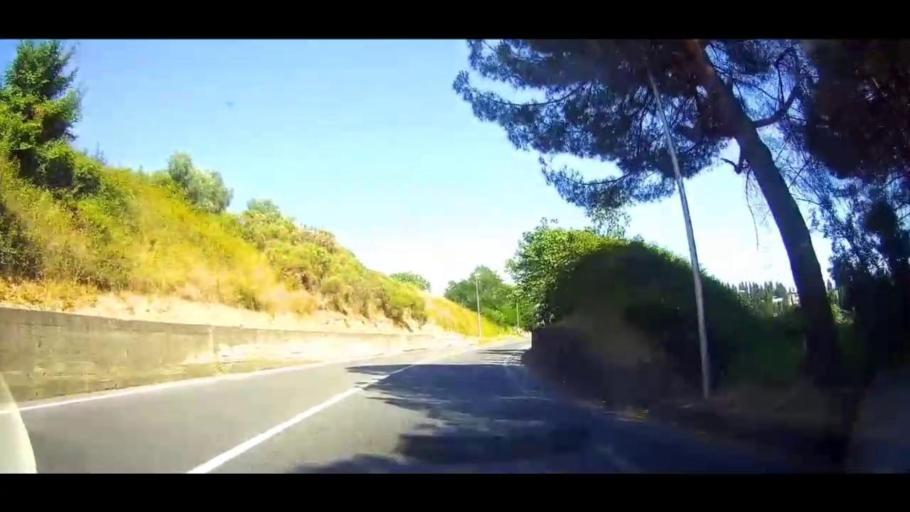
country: IT
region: Calabria
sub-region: Provincia di Cosenza
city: Cosenza
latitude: 39.2937
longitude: 16.2648
